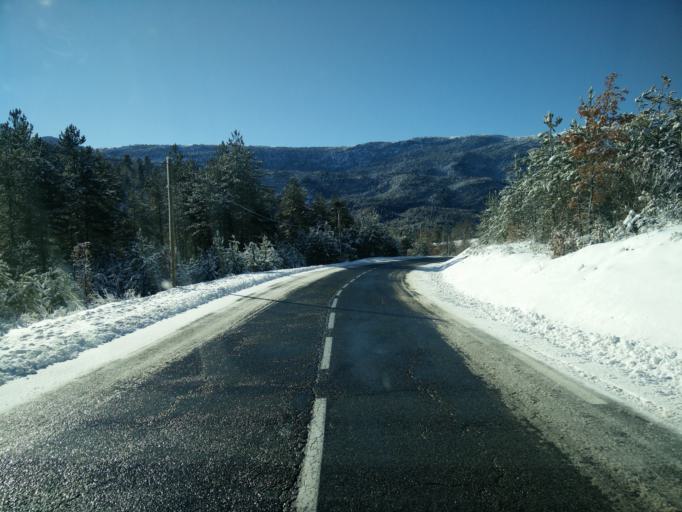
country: FR
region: Provence-Alpes-Cote d'Azur
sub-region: Departement des Alpes-de-Haute-Provence
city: Annot
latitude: 43.9172
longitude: 6.6094
